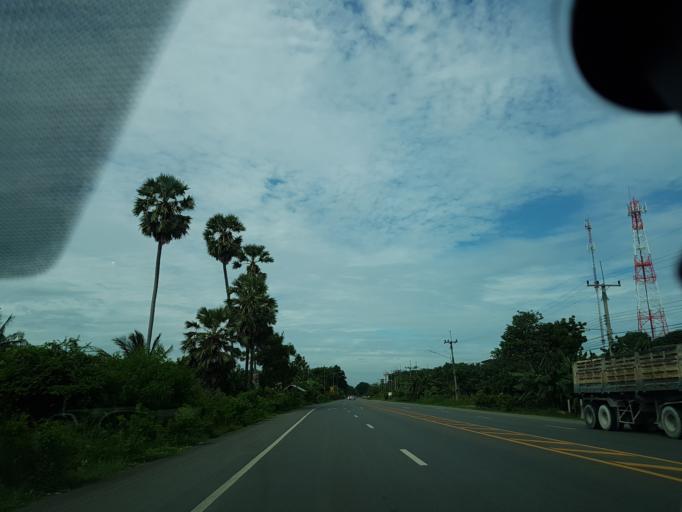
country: TH
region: Ang Thong
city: Chaiyo
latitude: 14.7256
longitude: 100.5016
